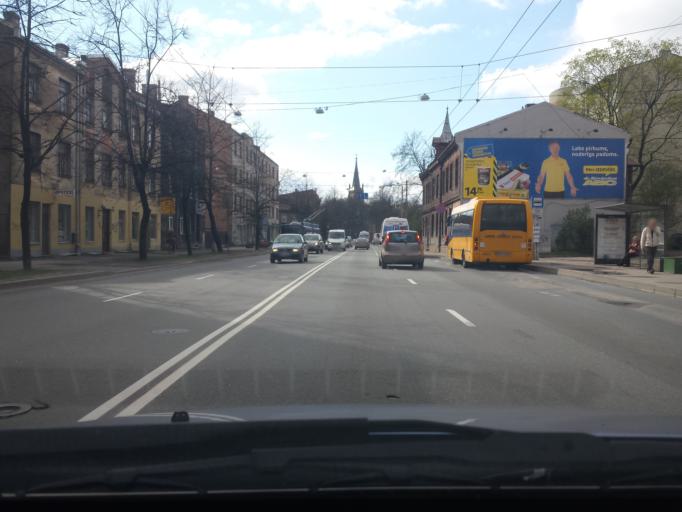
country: LV
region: Riga
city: Riga
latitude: 56.9532
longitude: 24.1558
